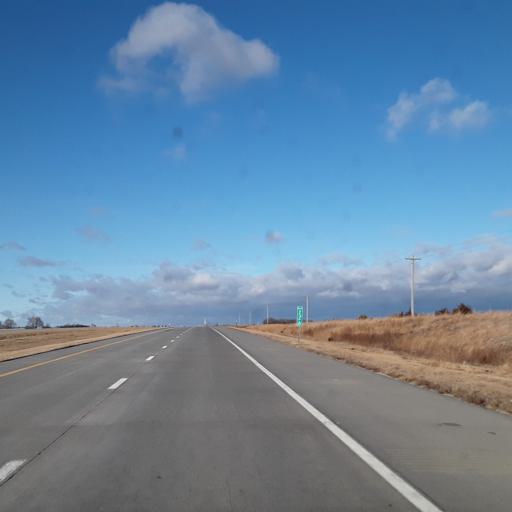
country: US
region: Kansas
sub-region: Republic County
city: Belleville
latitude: 39.8872
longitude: -97.6141
